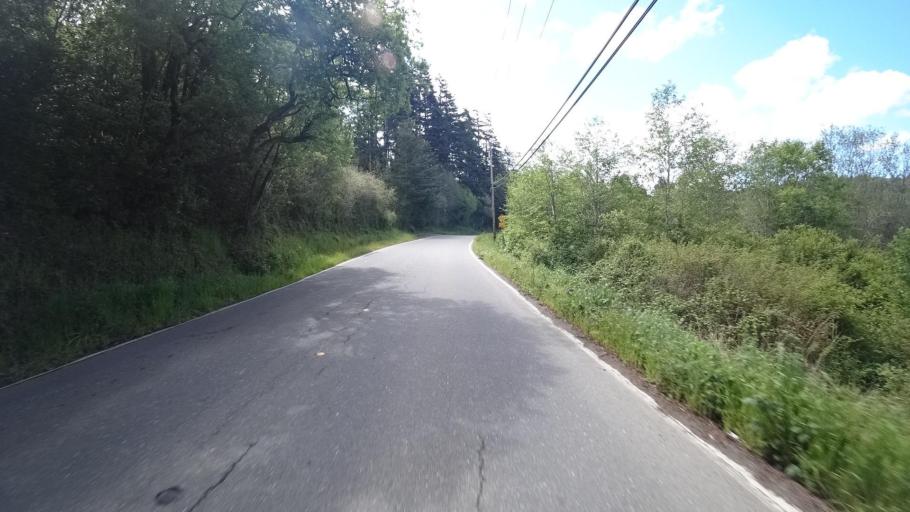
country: US
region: California
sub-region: Humboldt County
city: Blue Lake
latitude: 40.9054
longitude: -124.0253
